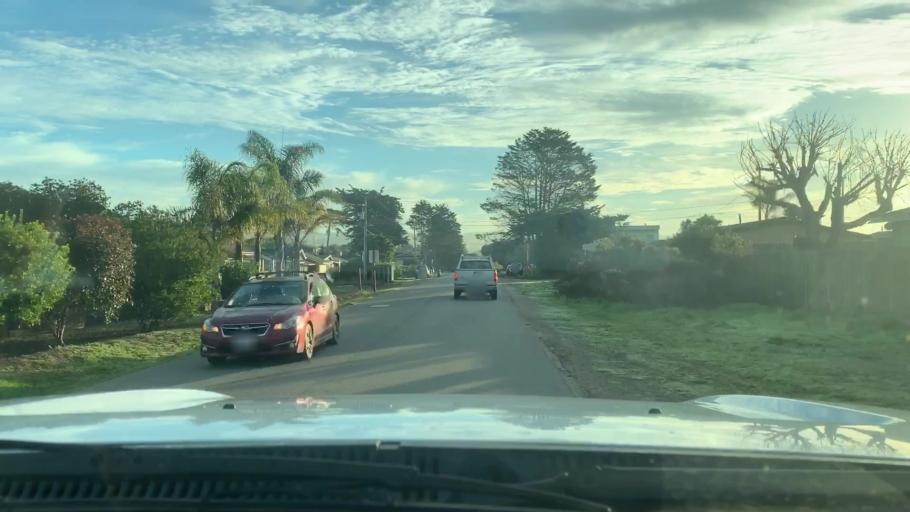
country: US
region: California
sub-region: San Luis Obispo County
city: Los Osos
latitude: 35.3243
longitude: -120.8264
